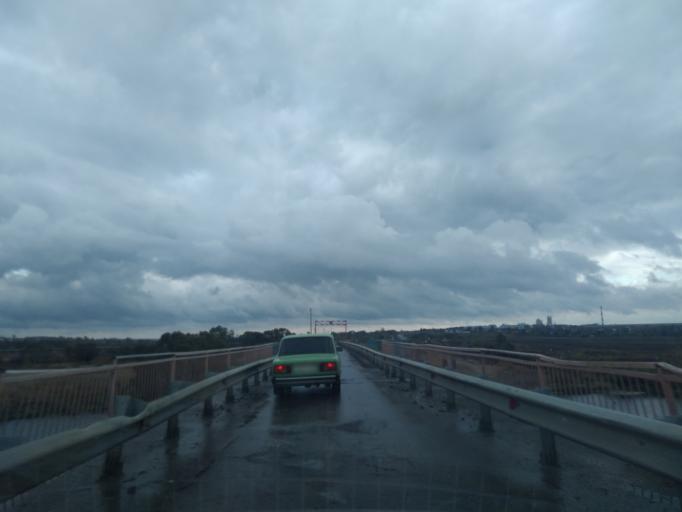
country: RU
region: Tula
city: Yefremov
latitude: 53.1301
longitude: 38.1198
